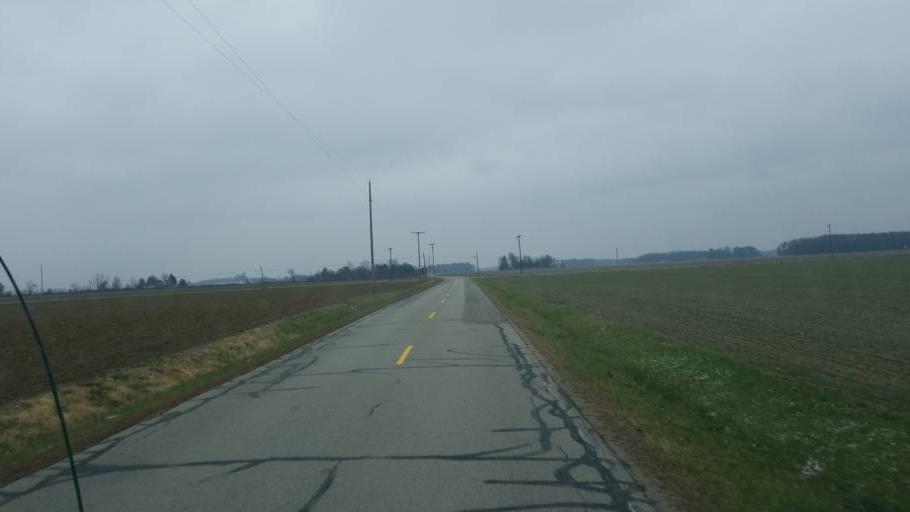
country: US
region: Ohio
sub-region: Crawford County
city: Crestline
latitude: 40.8285
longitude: -82.7663
